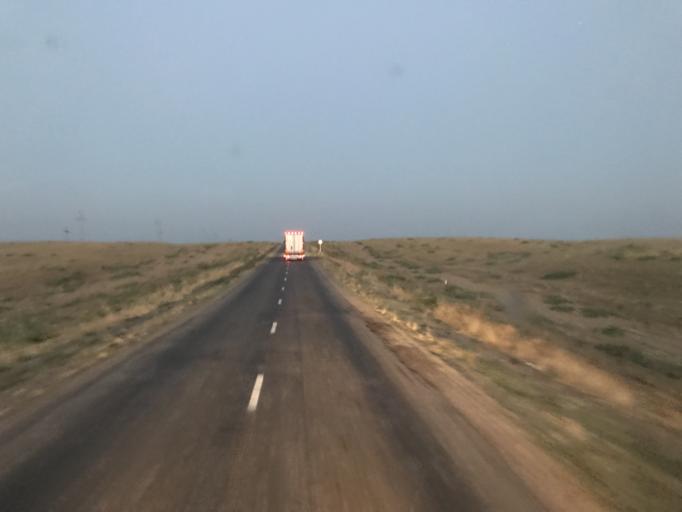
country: UZ
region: Toshkent
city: Chinoz
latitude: 41.1447
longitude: 68.6941
